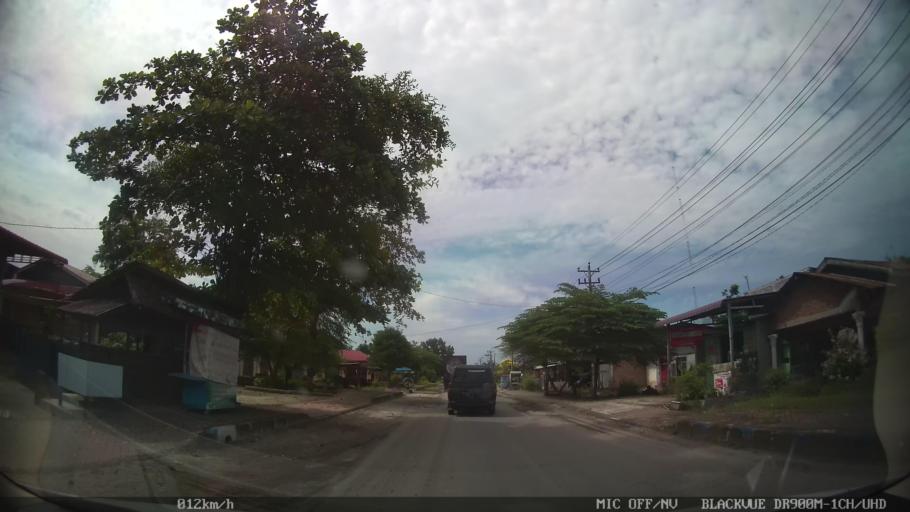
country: ID
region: North Sumatra
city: Percut
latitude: 3.5998
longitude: 98.8075
